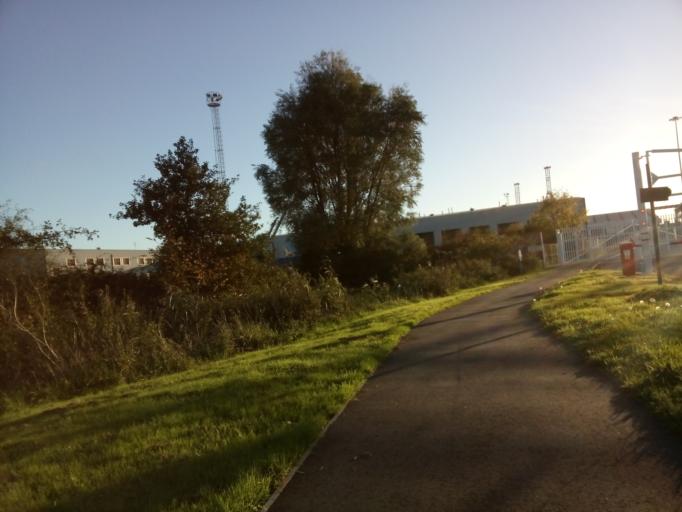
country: GB
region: England
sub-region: Essex
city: Harwich
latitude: 51.9593
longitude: 1.3144
